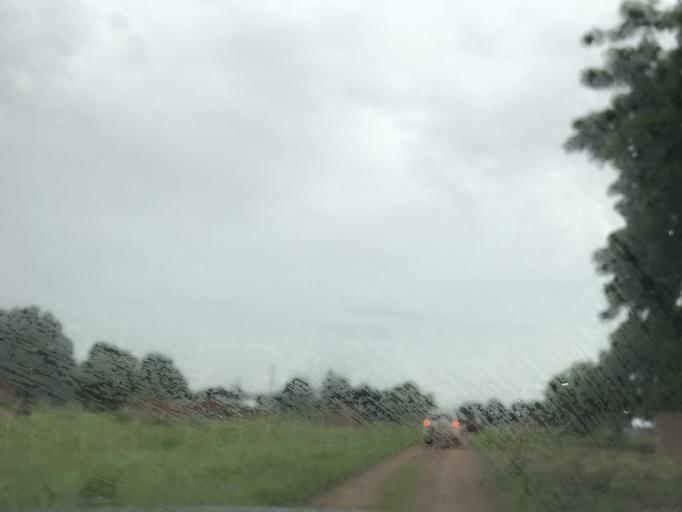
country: GH
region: Upper West
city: Wa
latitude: 10.5113
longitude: -2.7105
